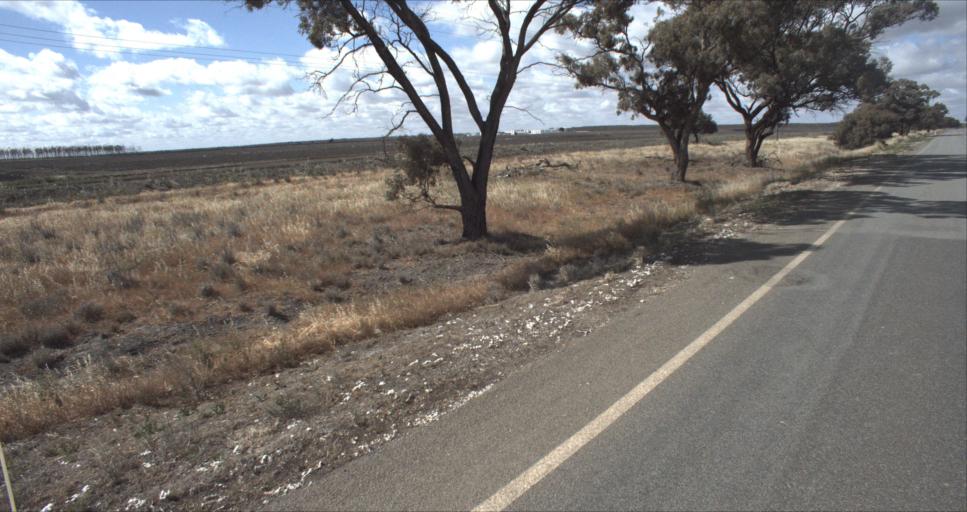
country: AU
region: New South Wales
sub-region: Murrumbidgee Shire
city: Darlington Point
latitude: -34.5617
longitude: 146.1689
